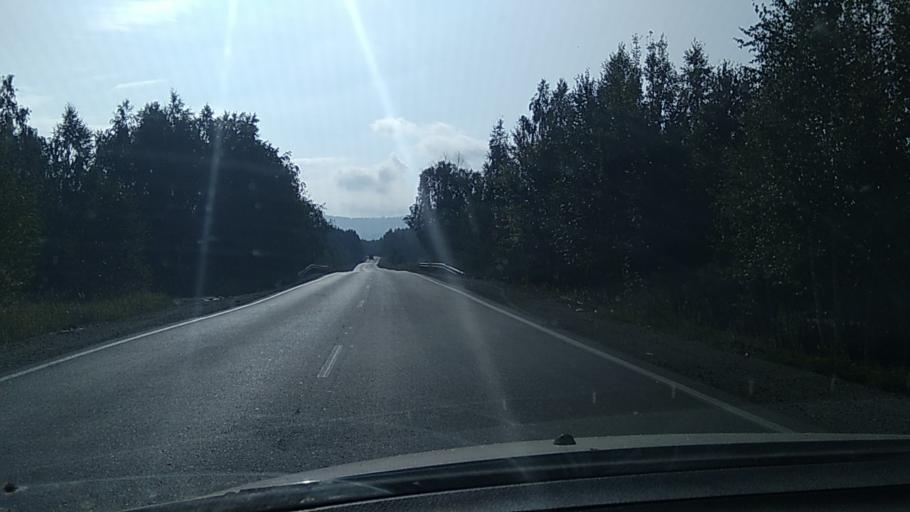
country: RU
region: Chelyabinsk
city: Karabash
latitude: 55.4339
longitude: 60.2477
